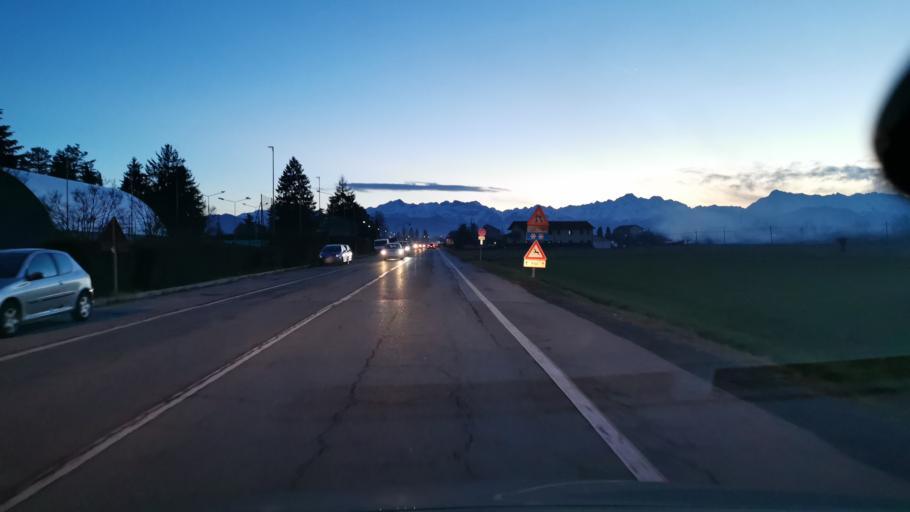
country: IT
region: Piedmont
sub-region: Provincia di Cuneo
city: Roata Rossi
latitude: 44.4396
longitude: 7.5636
